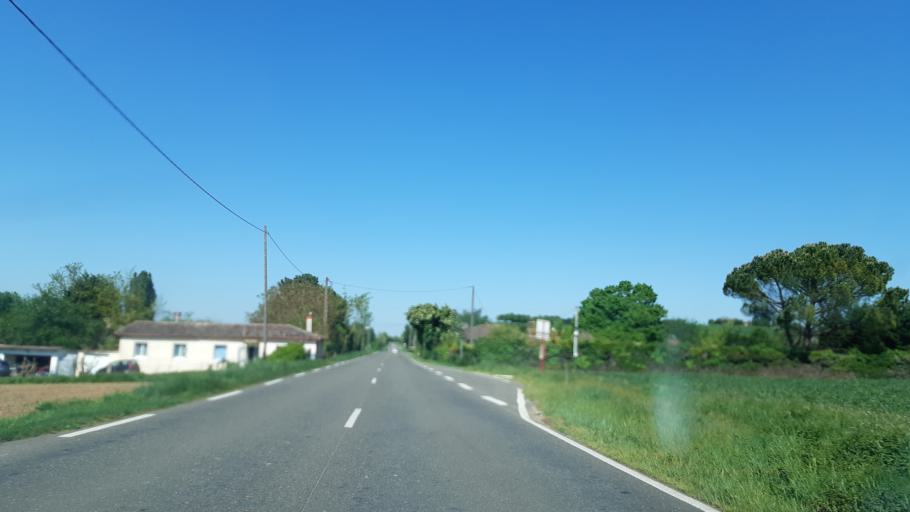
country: FR
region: Midi-Pyrenees
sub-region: Departement du Gers
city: Pujaudran
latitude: 43.5850
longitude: 1.0490
